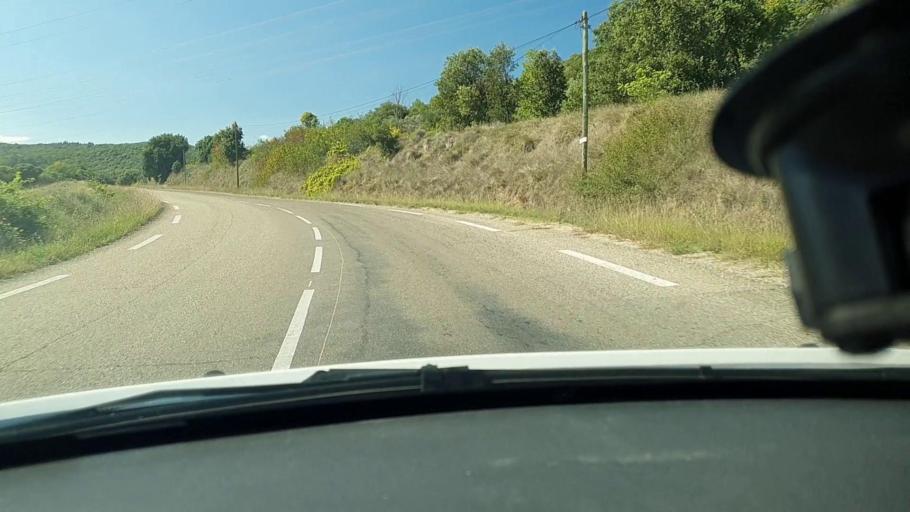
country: FR
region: Languedoc-Roussillon
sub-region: Departement du Gard
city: Saint-Paulet-de-Caisson
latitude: 44.2462
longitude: 4.5835
